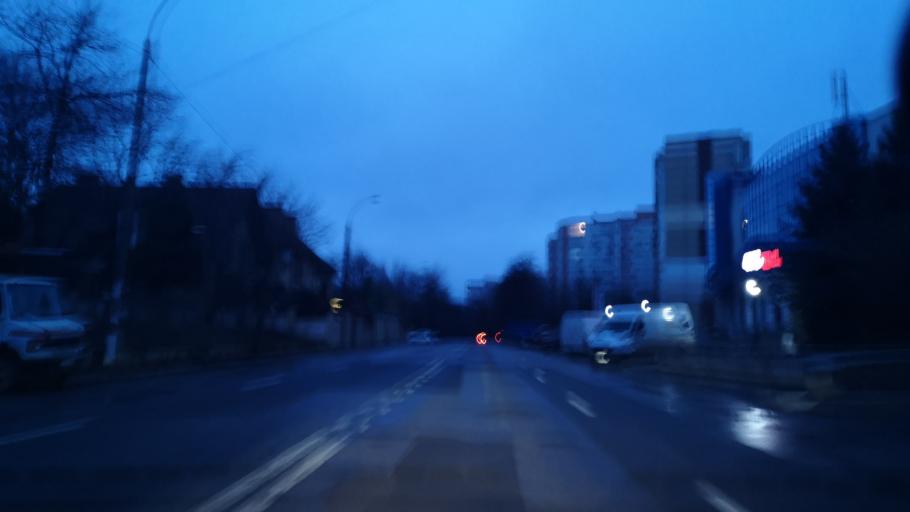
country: MD
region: Chisinau
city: Chisinau
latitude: 47.0371
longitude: 28.8789
